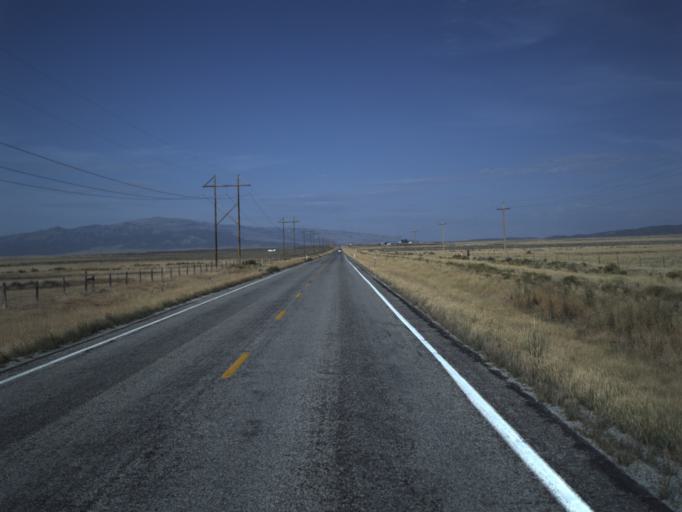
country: US
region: Idaho
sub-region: Oneida County
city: Malad City
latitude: 41.9661
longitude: -112.9644
